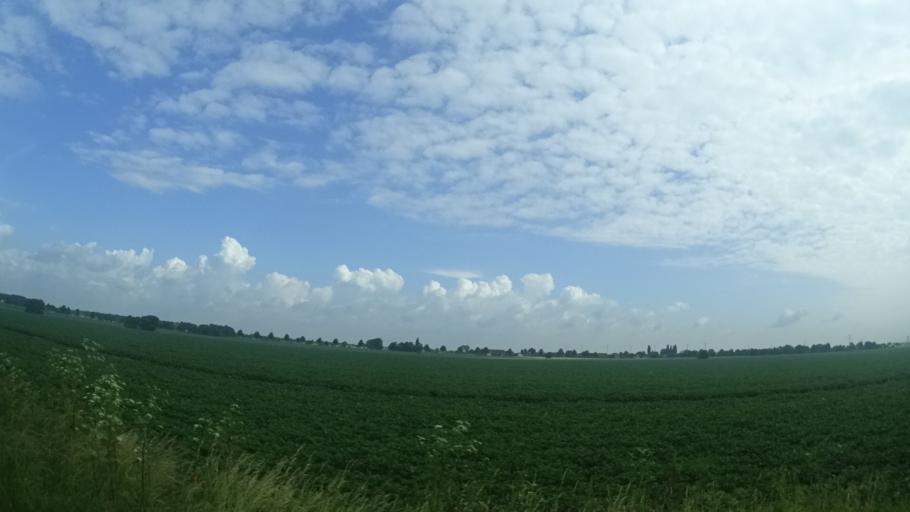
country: DE
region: Lower Saxony
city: Nordstemmen
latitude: 52.2073
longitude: 9.7546
